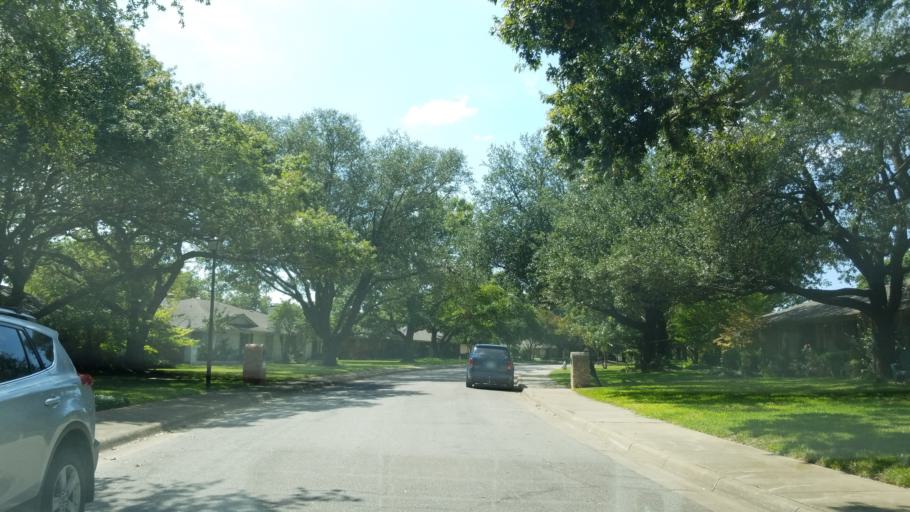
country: US
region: Texas
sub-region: Dallas County
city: Addison
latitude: 32.9526
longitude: -96.7877
